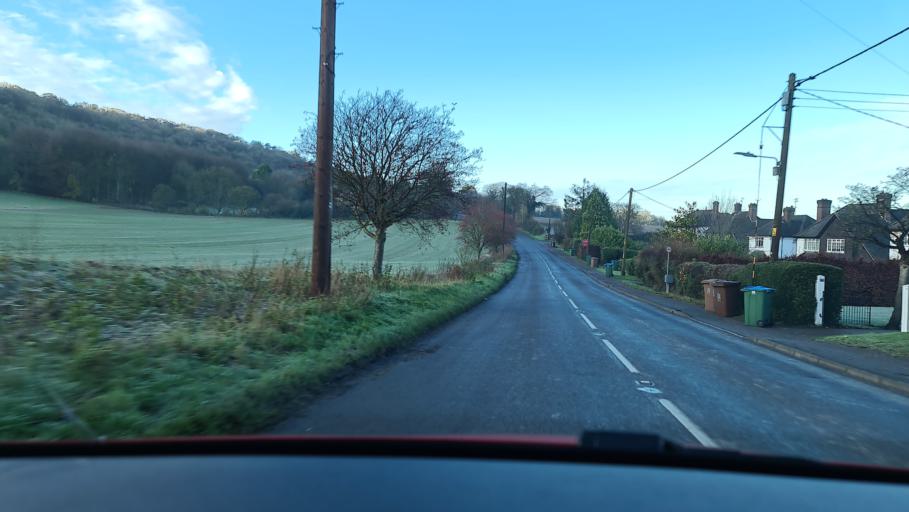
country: GB
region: England
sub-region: Buckinghamshire
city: Wendover
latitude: 51.7590
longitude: -0.7579
